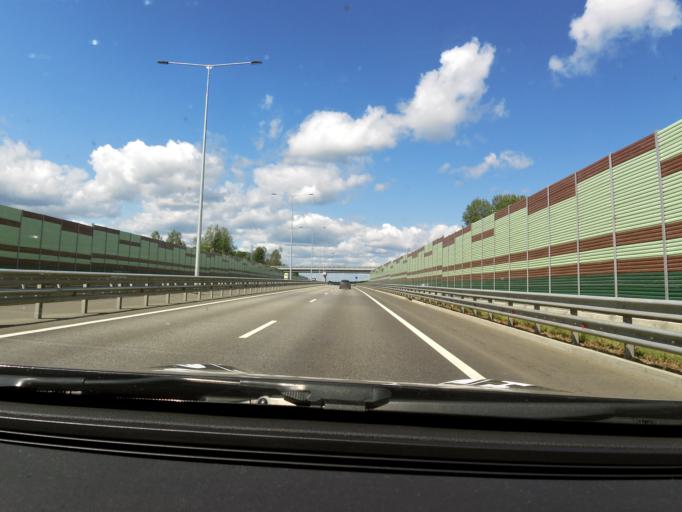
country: RU
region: Tverskaya
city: Vydropuzhsk
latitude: 57.3659
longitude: 34.6645
